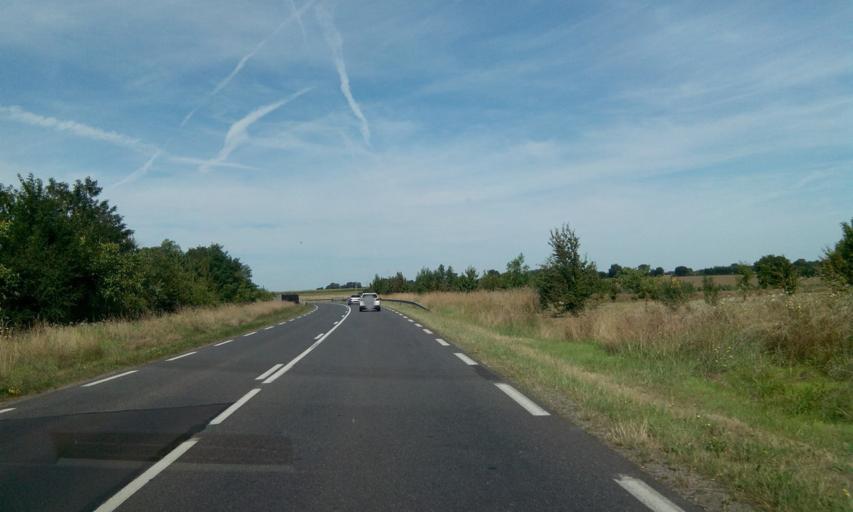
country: FR
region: Poitou-Charentes
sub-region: Departement de la Vienne
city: Charroux
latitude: 46.1523
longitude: 0.4012
